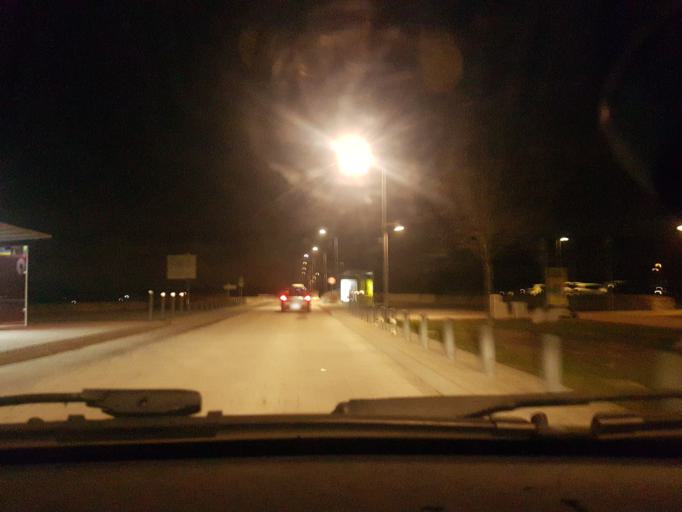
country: FR
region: Franche-Comte
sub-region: Territoire de Belfort
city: Bourogne
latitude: 47.5845
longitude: 6.8963
